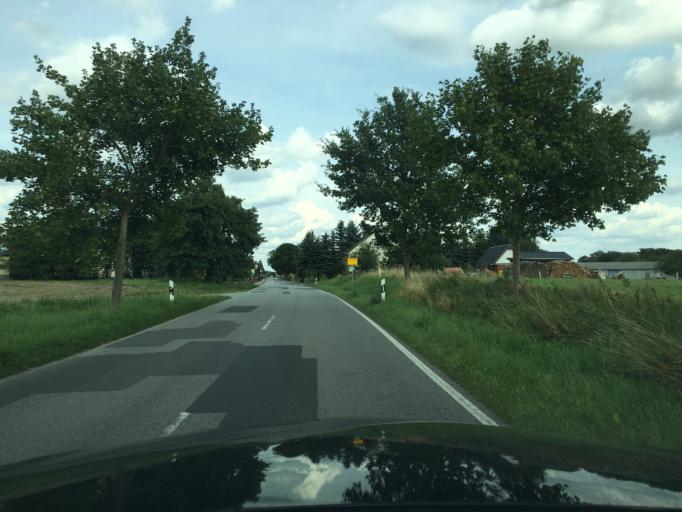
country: DE
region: Mecklenburg-Vorpommern
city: Penzlin
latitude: 53.4815
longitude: 13.0271
